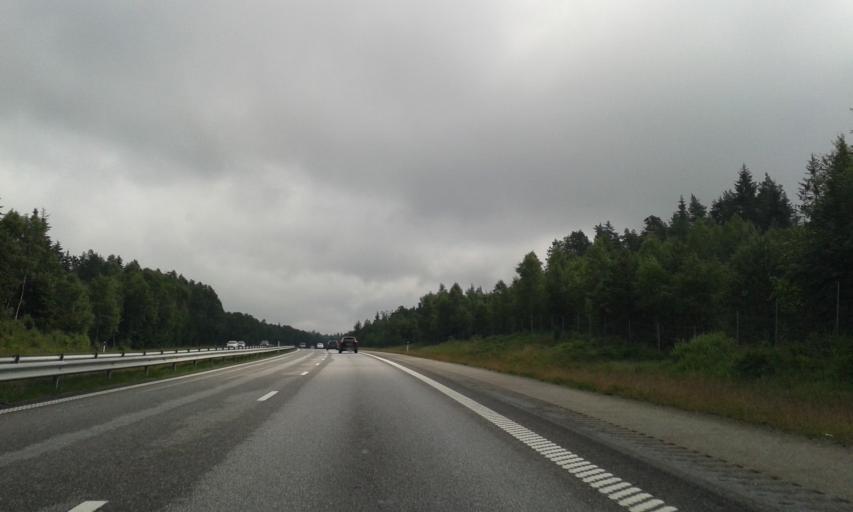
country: SE
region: Vaestra Goetaland
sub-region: Harryda Kommun
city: Hindas
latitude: 57.6675
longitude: 12.4133
